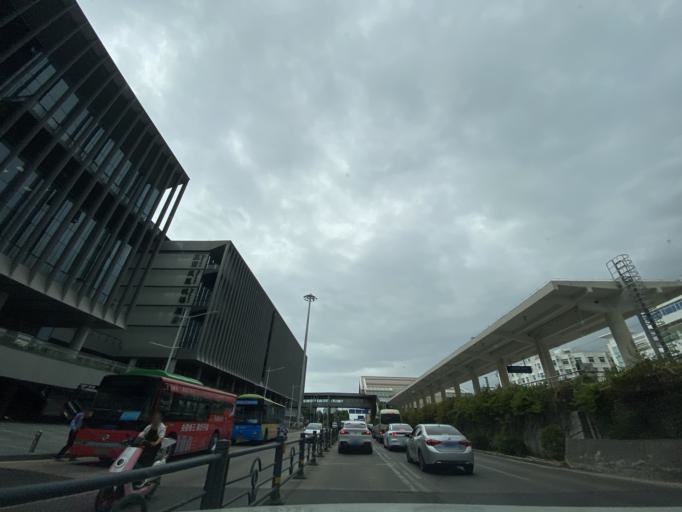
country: CN
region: Hainan
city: Fenghuang
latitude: 18.3106
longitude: 109.4069
